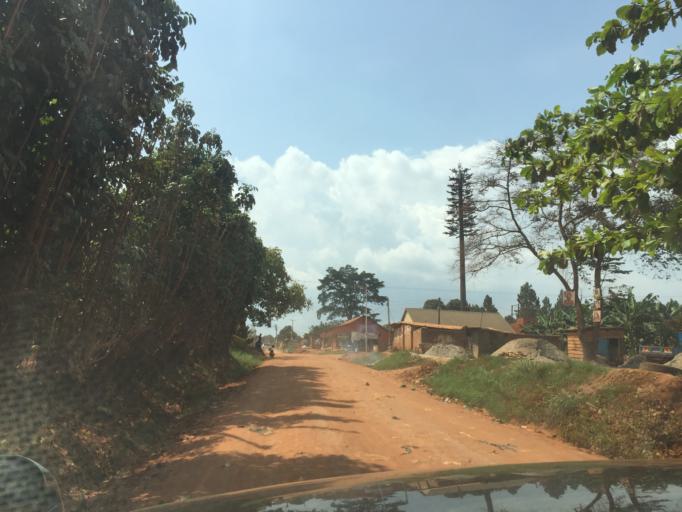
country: UG
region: Central Region
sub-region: Wakiso District
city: Kireka
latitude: 0.3987
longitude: 32.6221
